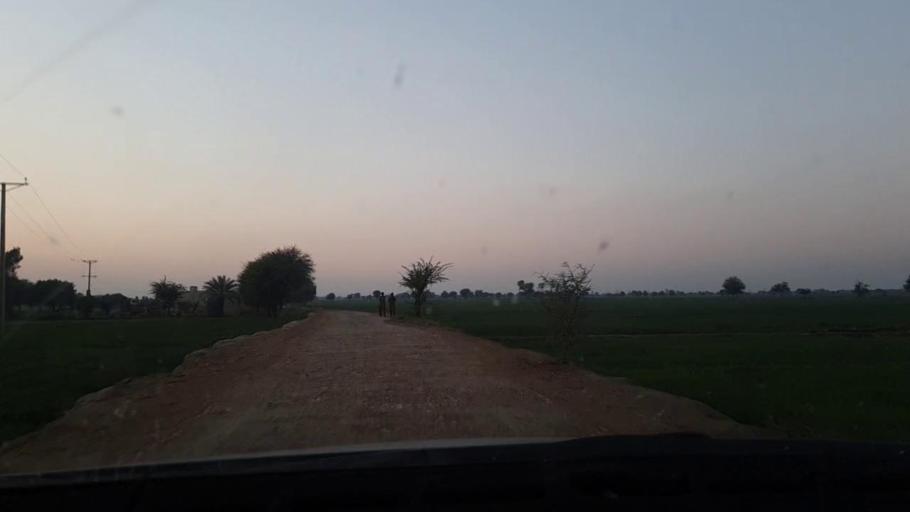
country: PK
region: Sindh
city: Tando Mittha Khan
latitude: 25.9298
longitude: 69.3296
